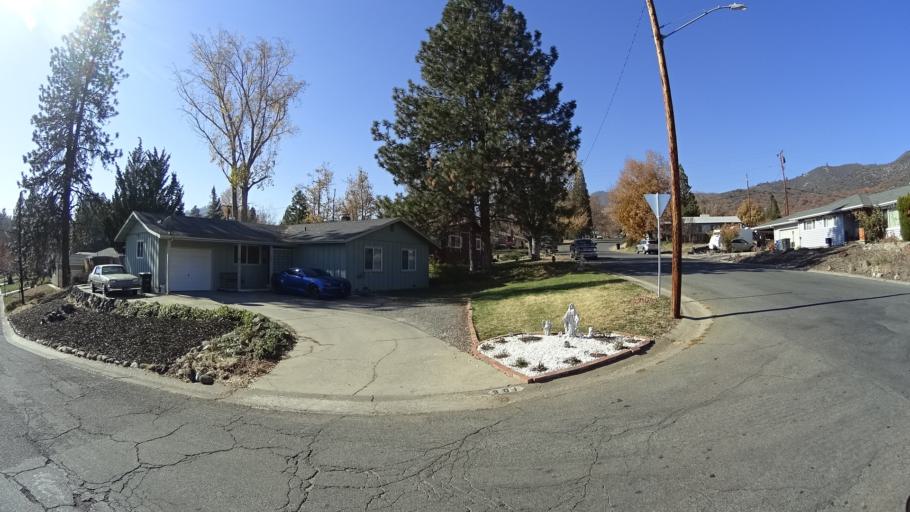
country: US
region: California
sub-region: Siskiyou County
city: Yreka
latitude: 41.7417
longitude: -122.6449
